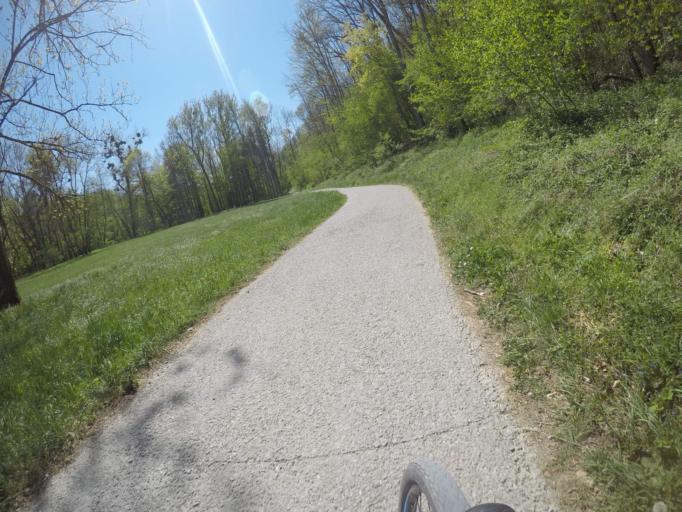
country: DE
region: Baden-Wuerttemberg
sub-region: Regierungsbezirk Stuttgart
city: Waiblingen
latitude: 48.8694
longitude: 9.2979
